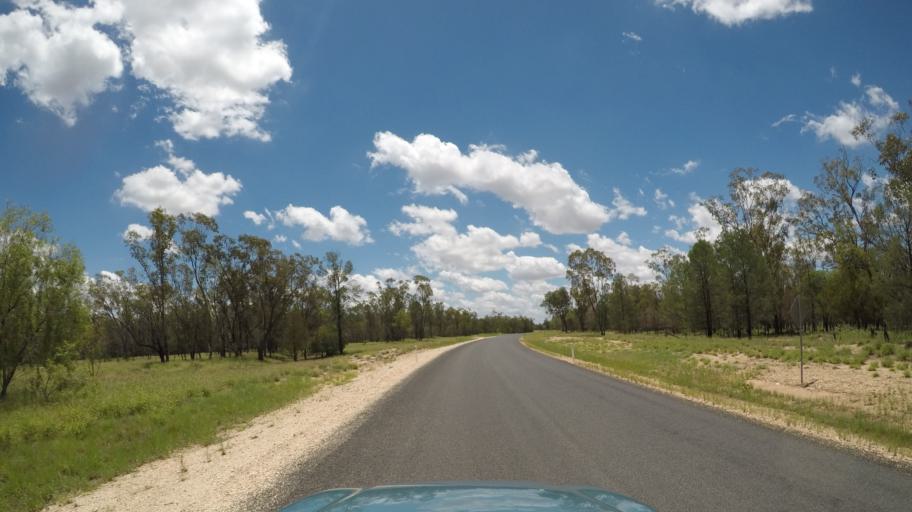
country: AU
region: Queensland
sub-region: Goondiwindi
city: Goondiwindi
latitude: -28.1573
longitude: 150.1200
